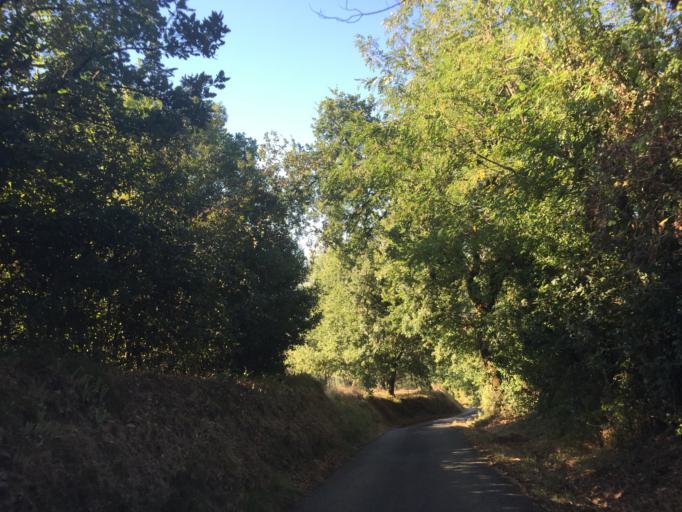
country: IT
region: Tuscany
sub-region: Provincia di Pistoia
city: Pistoia
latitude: 43.9592
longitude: 10.9407
